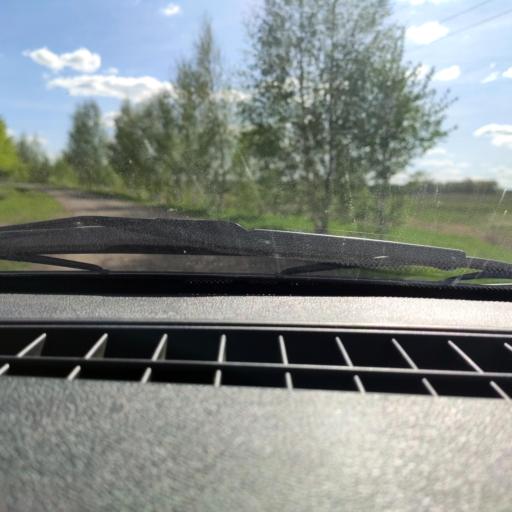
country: RU
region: Bashkortostan
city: Avdon
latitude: 54.6984
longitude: 55.7898
